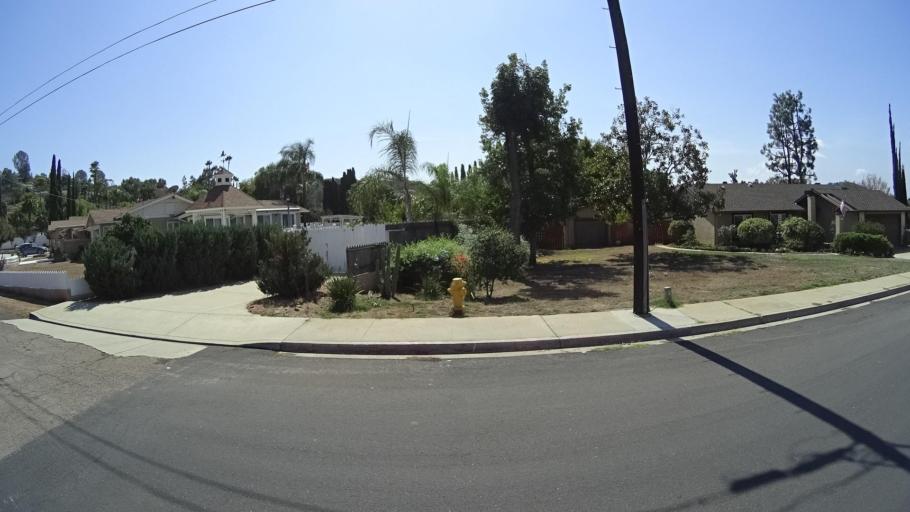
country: US
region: California
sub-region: San Diego County
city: Granite Hills
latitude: 32.7847
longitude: -116.9178
